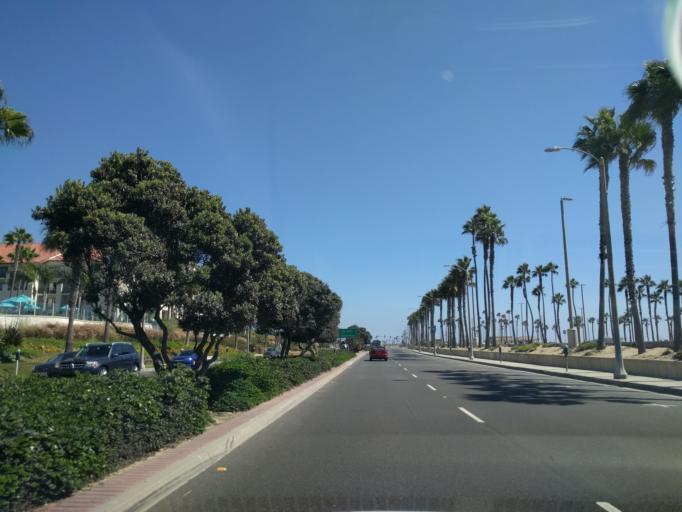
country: US
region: California
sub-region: Orange County
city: Huntington Beach
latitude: 33.6502
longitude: -117.9909
